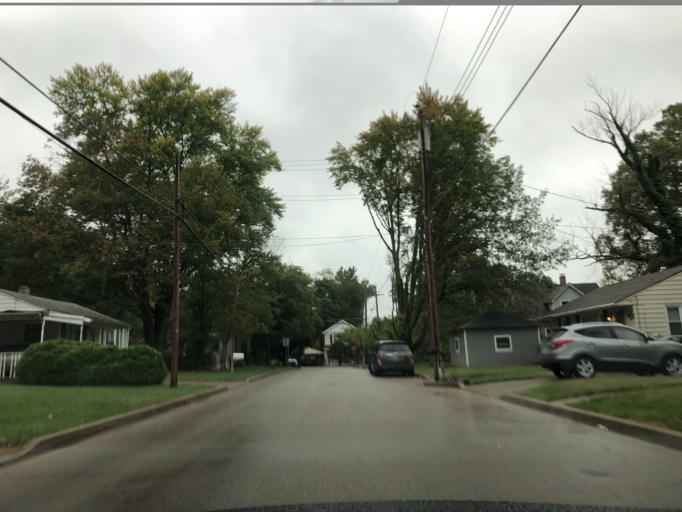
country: US
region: Ohio
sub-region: Hamilton County
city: Loveland
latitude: 39.2596
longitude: -84.2509
